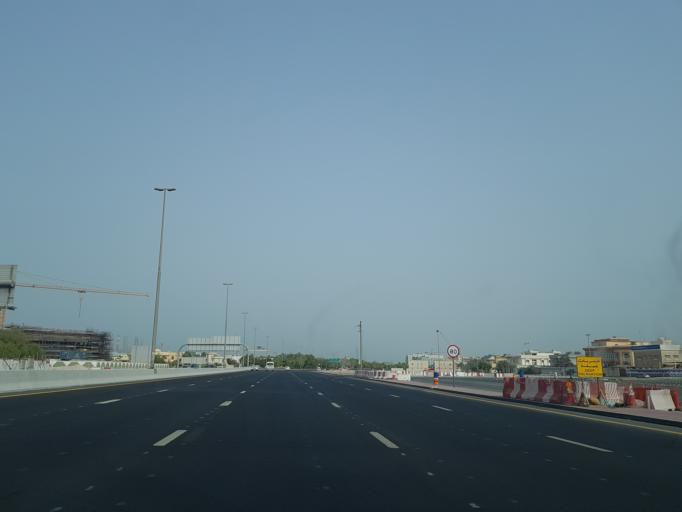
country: AE
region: Ash Shariqah
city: Sharjah
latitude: 25.2426
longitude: 55.2901
